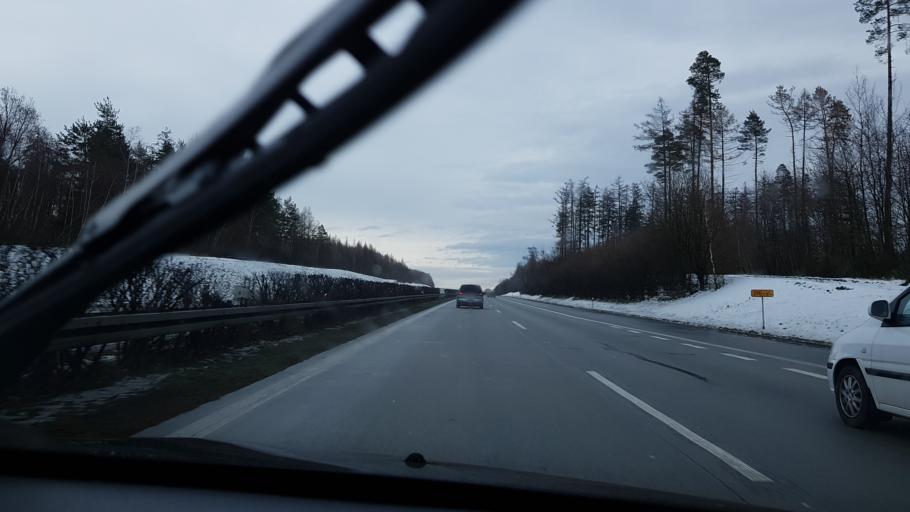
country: CZ
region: Olomoucky
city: Velky Ujezd
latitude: 49.5649
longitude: 17.5042
